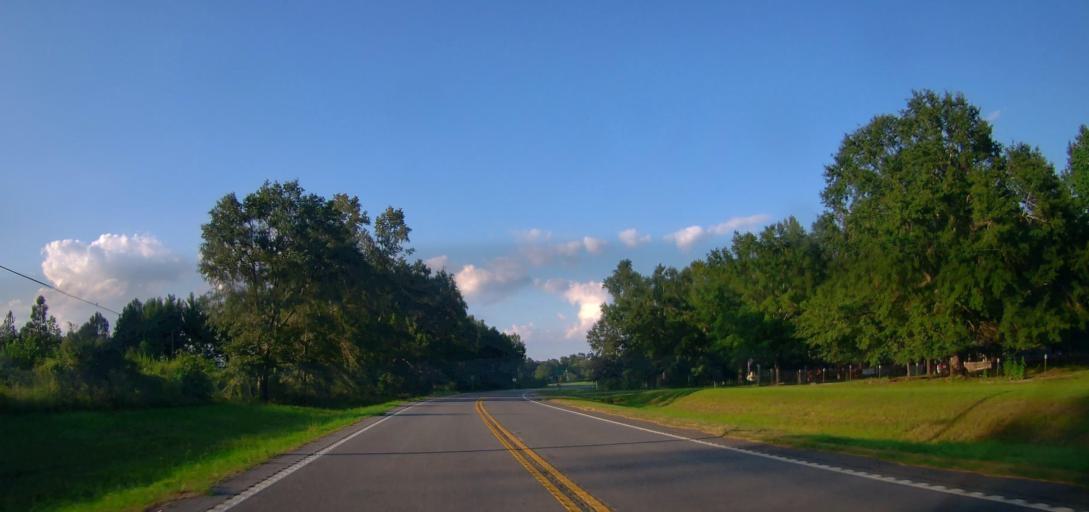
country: US
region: Georgia
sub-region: Taylor County
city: Reynolds
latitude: 32.6627
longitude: -84.1055
